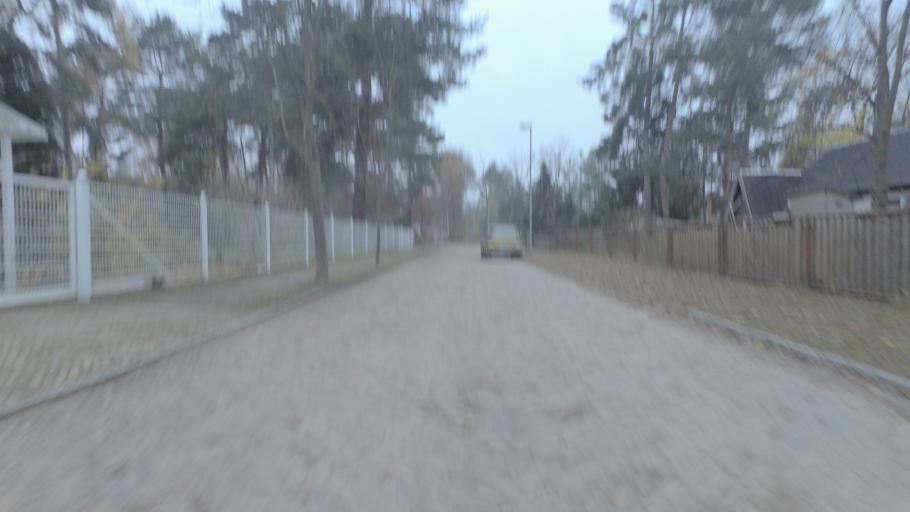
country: DE
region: Brandenburg
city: Am Mellensee
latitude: 52.1687
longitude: 13.3905
